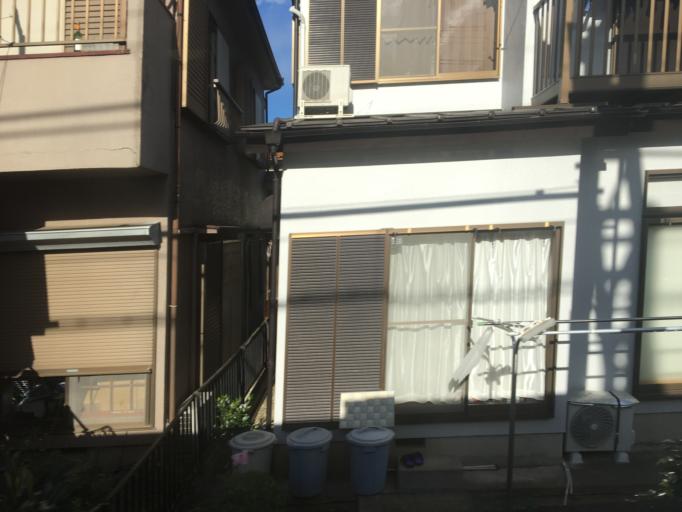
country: JP
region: Saitama
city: Ogawa
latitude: 36.0420
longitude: 139.3334
